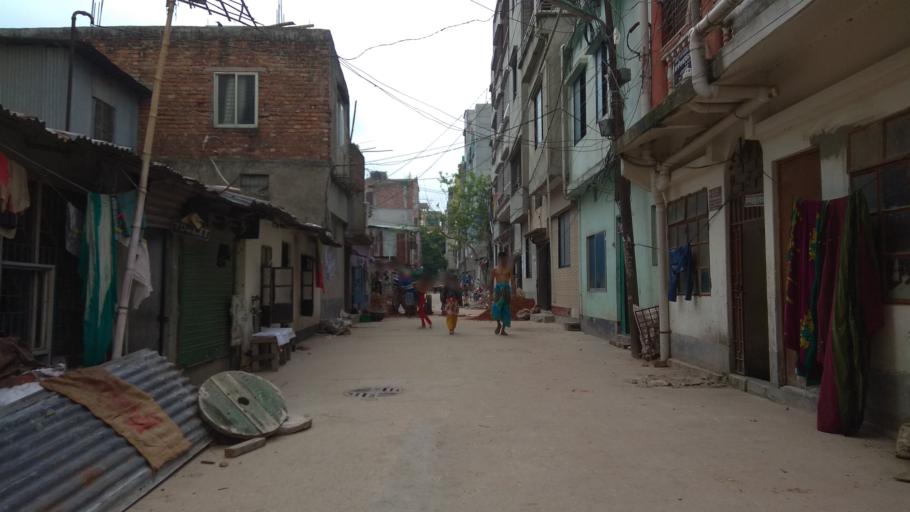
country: BD
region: Dhaka
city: Tungi
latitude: 23.8234
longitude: 90.3550
